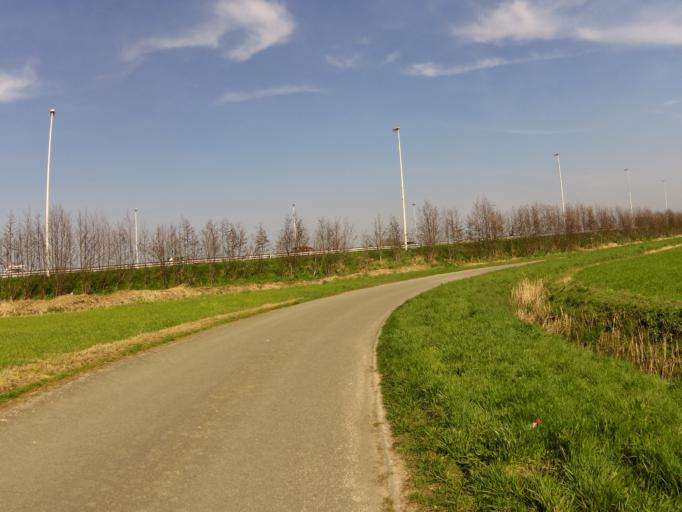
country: BE
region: Flanders
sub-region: Provincie West-Vlaanderen
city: Oudenburg
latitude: 51.1729
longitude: 2.9996
